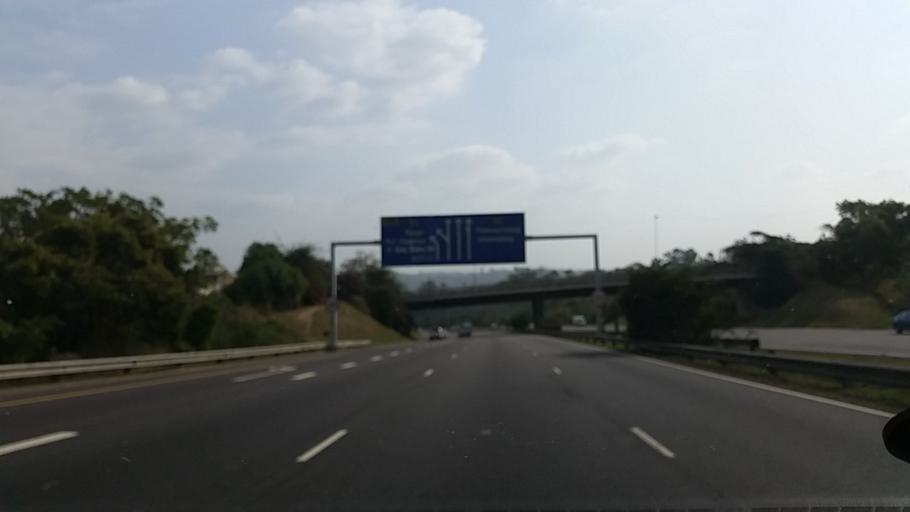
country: ZA
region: KwaZulu-Natal
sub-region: eThekwini Metropolitan Municipality
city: Berea
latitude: -29.8395
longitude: 30.9678
